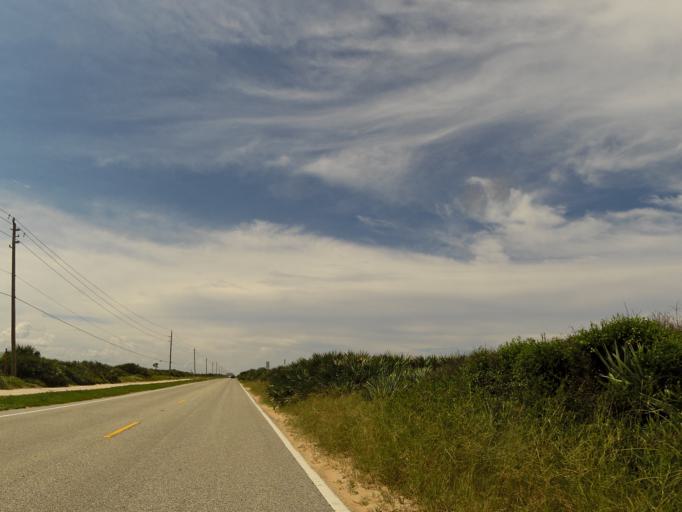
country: US
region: Florida
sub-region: Volusia County
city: Ormond-by-the-Sea
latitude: 29.3973
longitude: -81.0891
